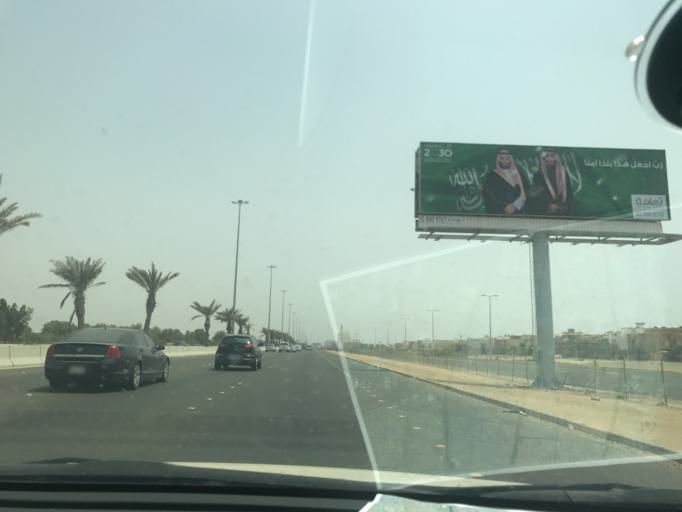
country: SA
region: Makkah
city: Jeddah
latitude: 21.6941
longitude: 39.1195
